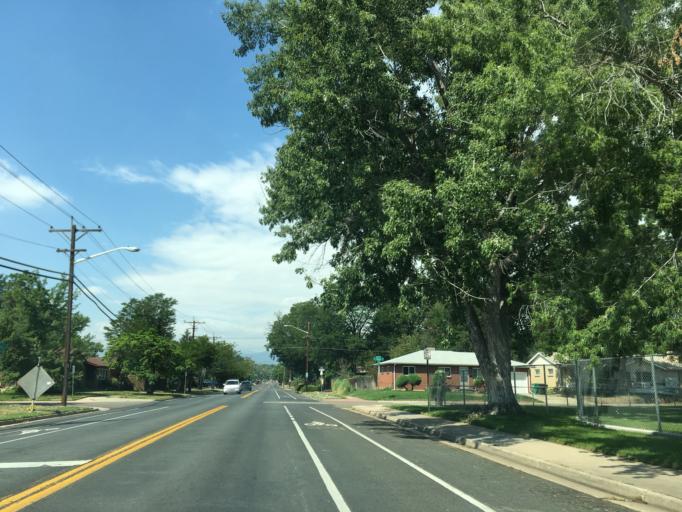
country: US
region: Colorado
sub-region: Arapahoe County
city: Sheridan
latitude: 39.6585
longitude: -105.0454
